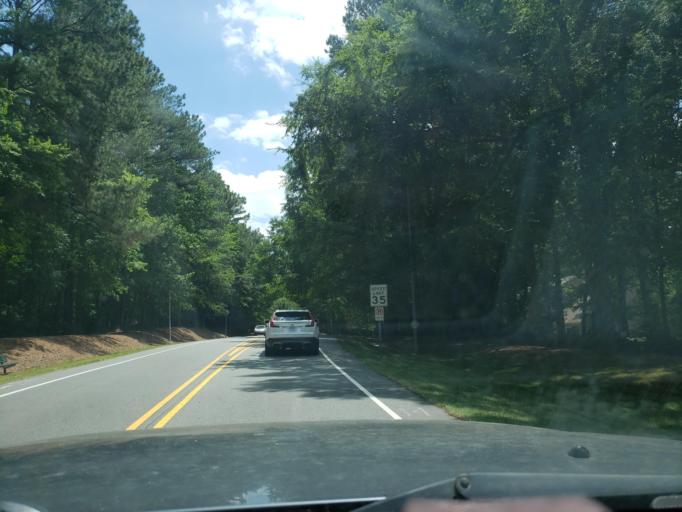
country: US
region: North Carolina
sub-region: Durham County
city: Durham
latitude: 35.9242
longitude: -78.9444
